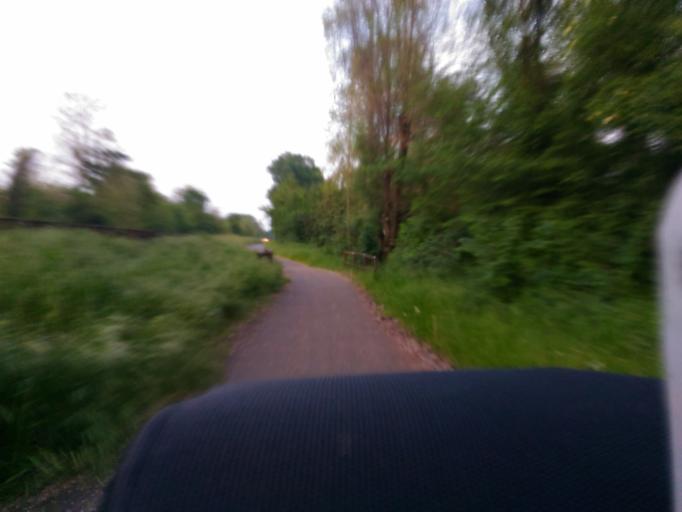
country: IT
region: Lombardy
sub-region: Provincia di Lodi
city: Muzza di Cornegliano Laudense
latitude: 45.3061
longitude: 9.4570
